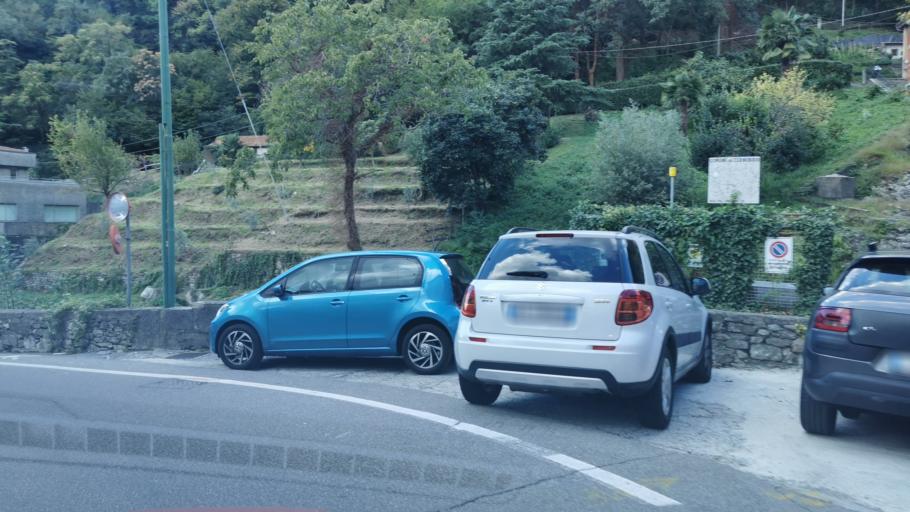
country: IT
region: Lombardy
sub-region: Provincia di Como
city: Cernobbio
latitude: 45.8440
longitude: 9.0733
